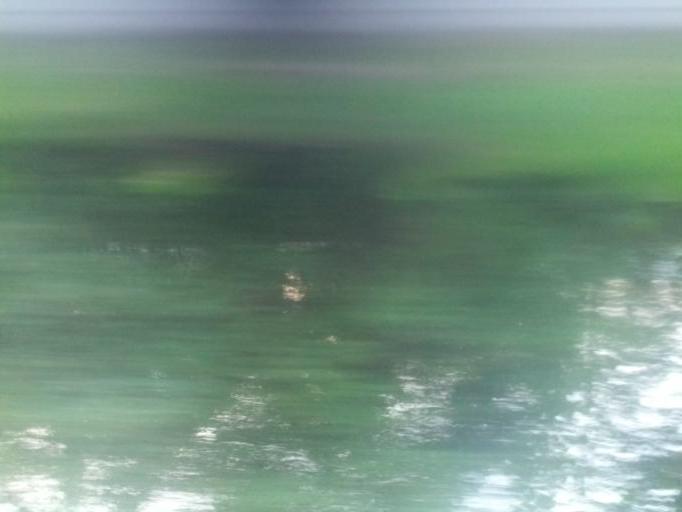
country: RU
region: St.-Petersburg
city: Staraya Derevnya
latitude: 59.9933
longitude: 30.2555
